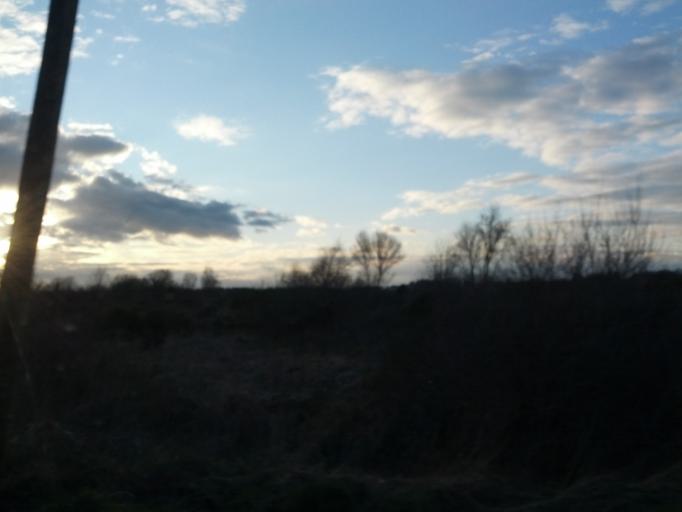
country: IE
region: Connaught
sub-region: County Galway
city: Athenry
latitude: 53.3282
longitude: -8.7023
